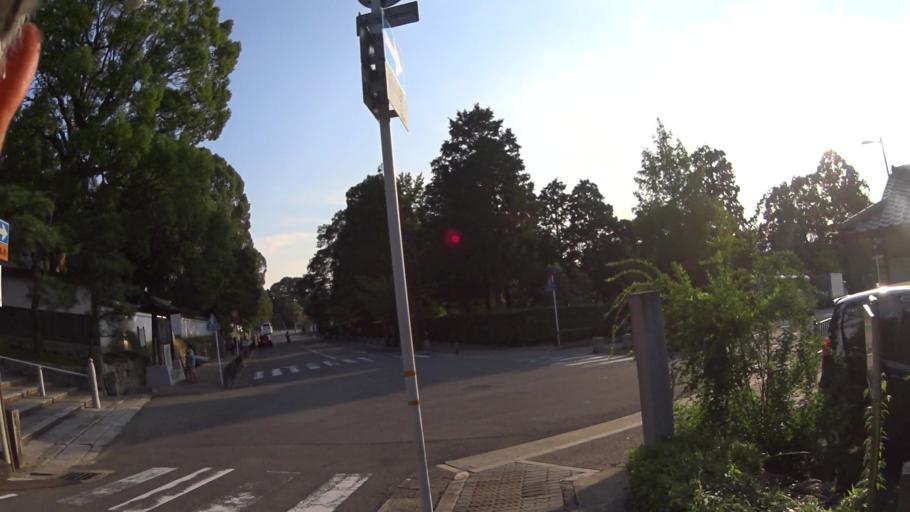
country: JP
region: Kyoto
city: Kyoto
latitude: 35.0067
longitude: 135.7822
